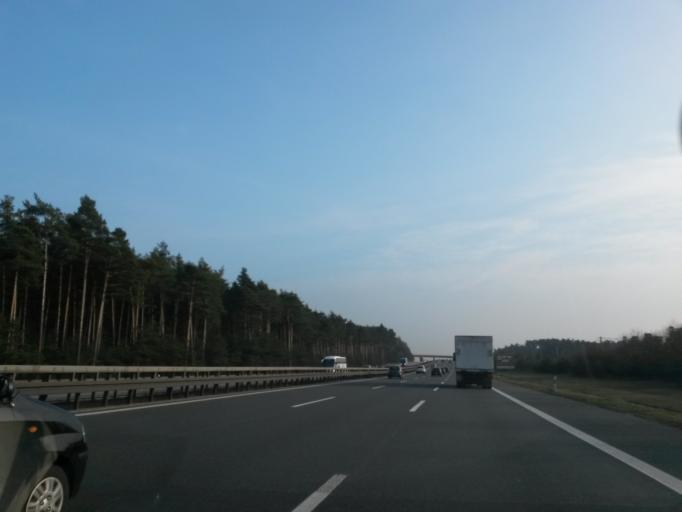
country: DE
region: Bavaria
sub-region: Regierungsbezirk Mittelfranken
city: Allersberg
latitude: 49.2850
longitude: 11.2088
